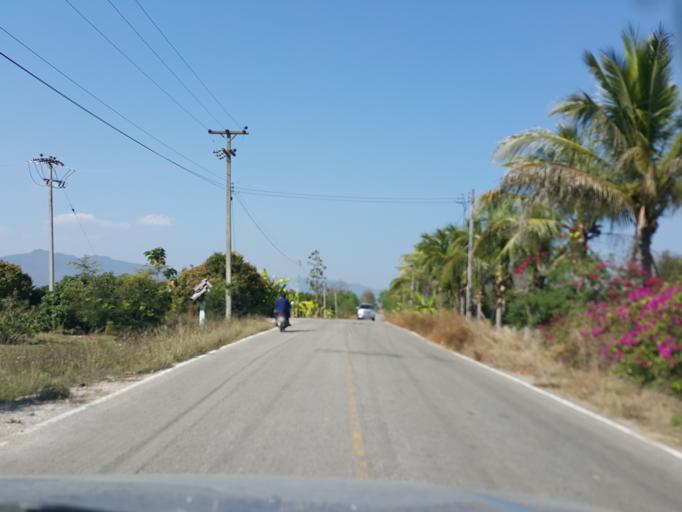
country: TH
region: Chiang Mai
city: Mae Wang
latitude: 18.5644
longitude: 98.7924
